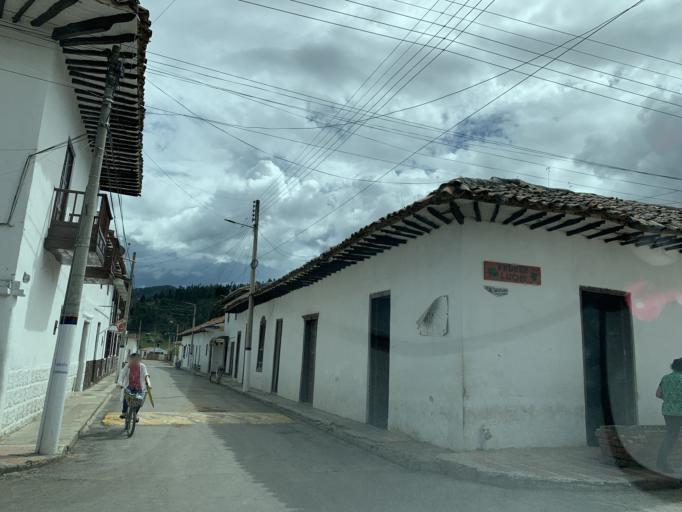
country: CO
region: Boyaca
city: Floresta
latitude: 5.8601
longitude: -72.9193
